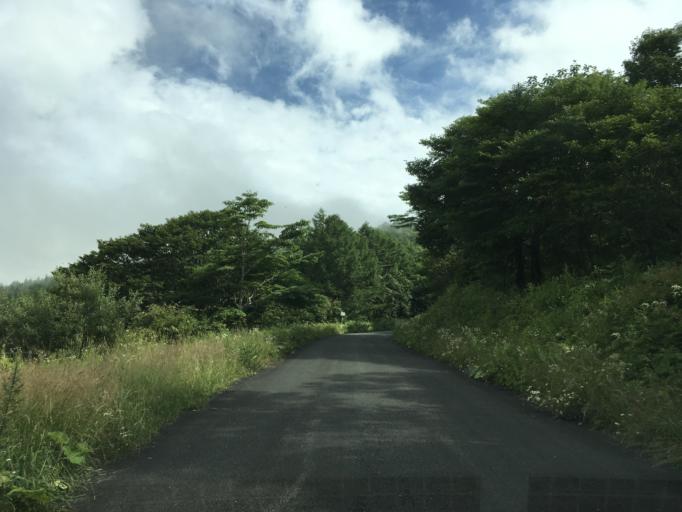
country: JP
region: Iwate
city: Ofunato
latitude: 38.9797
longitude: 141.4528
